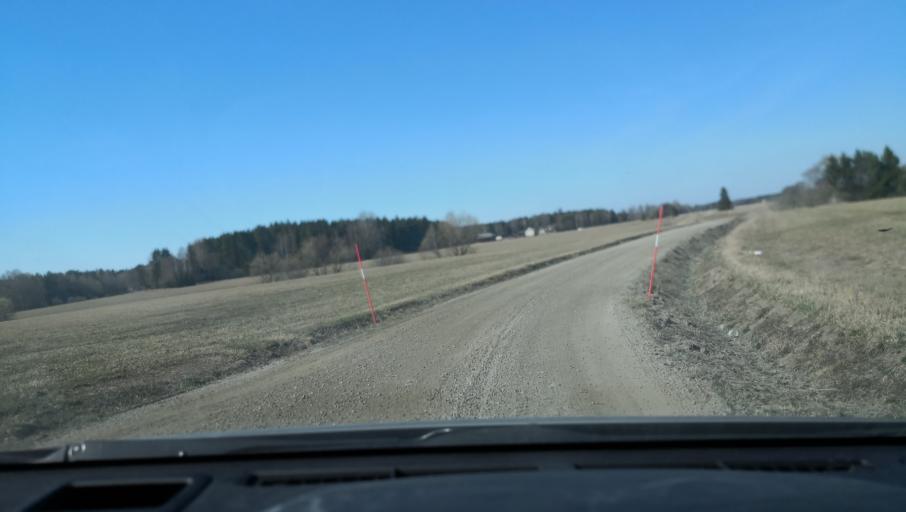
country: SE
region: Vaestmanland
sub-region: Sala Kommun
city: Sala
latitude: 59.8775
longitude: 16.5328
